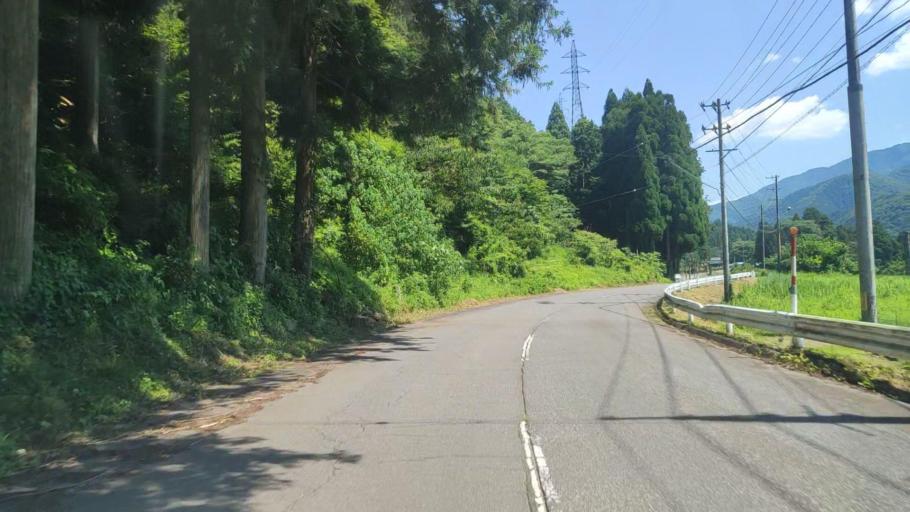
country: JP
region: Gifu
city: Godo
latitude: 35.6748
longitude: 136.5751
